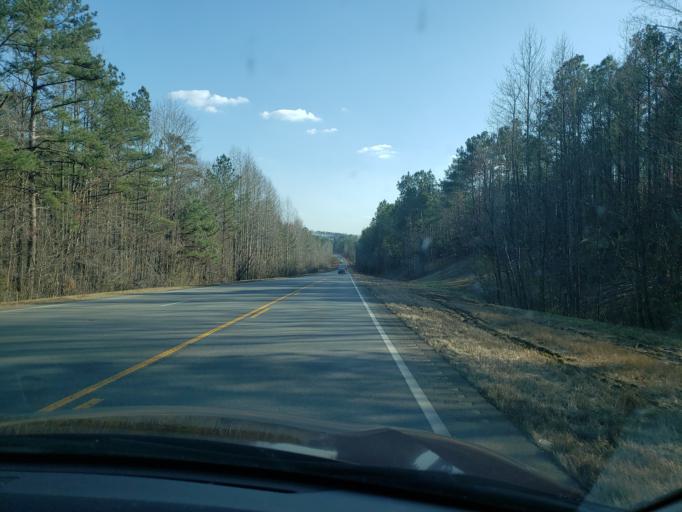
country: US
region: Alabama
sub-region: Randolph County
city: Wedowee
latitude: 33.4575
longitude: -85.5729
